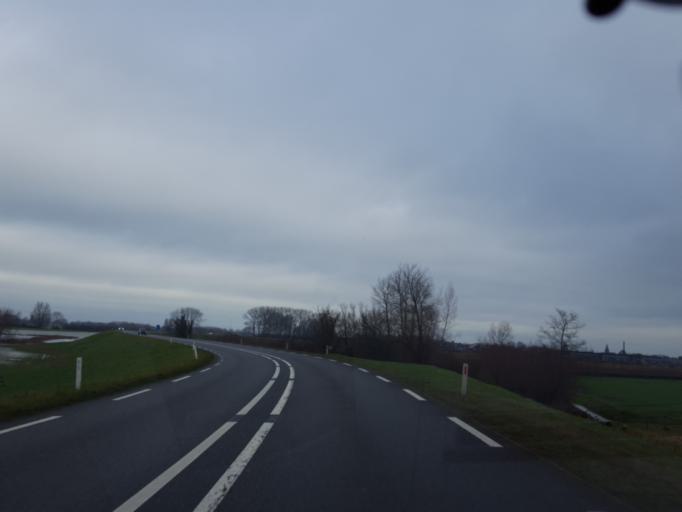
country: NL
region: Overijssel
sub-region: Gemeente Olst-Wijhe
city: Olst
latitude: 52.3226
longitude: 6.1013
